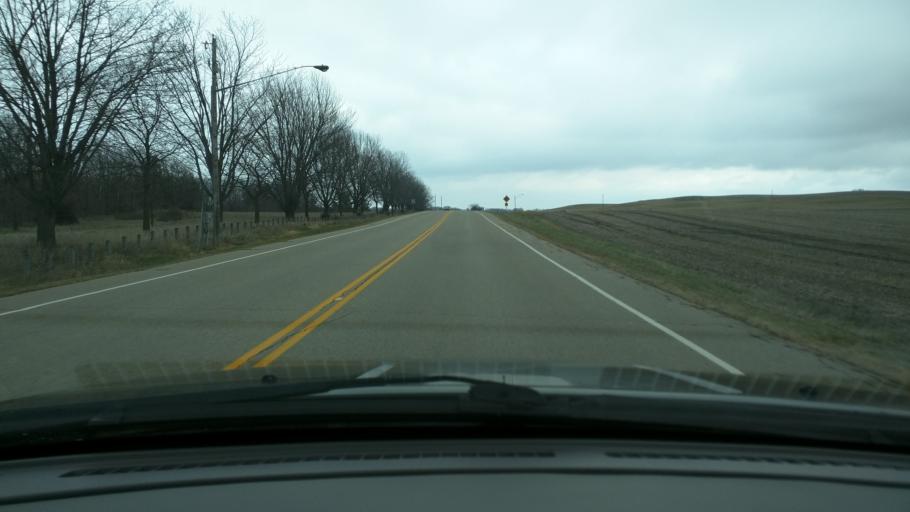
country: US
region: Minnesota
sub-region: Washington County
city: Cottage Grove
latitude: 44.7639
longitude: -92.9287
